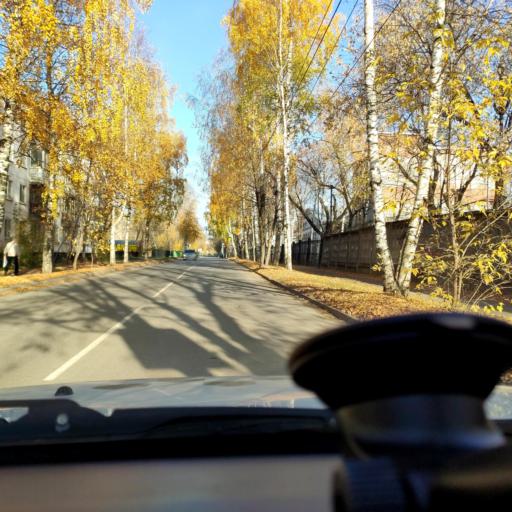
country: RU
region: Perm
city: Perm
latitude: 58.0120
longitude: 56.2916
